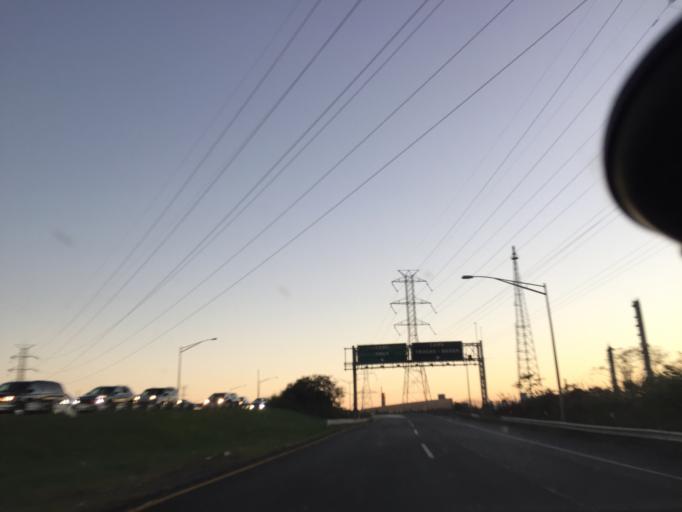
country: US
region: New Jersey
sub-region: Union County
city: Elizabeth
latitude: 40.6395
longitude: -74.2079
